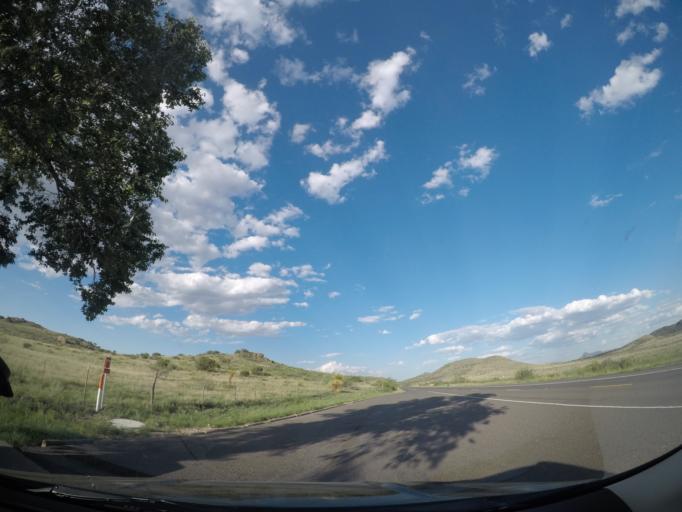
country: US
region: Texas
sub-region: Brewster County
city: Alpine
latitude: 30.2687
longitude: -103.8167
